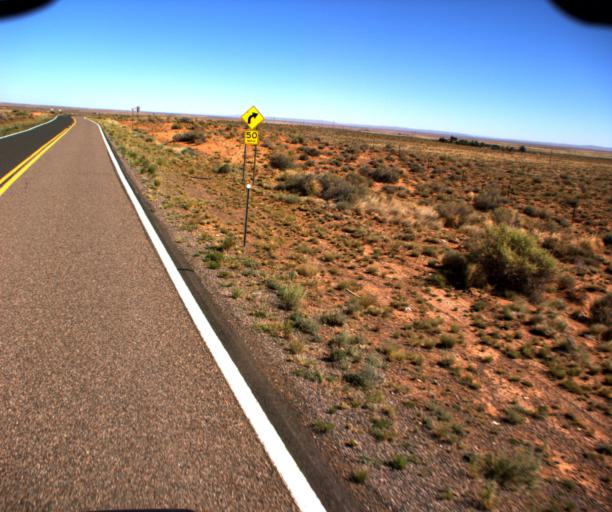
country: US
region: Arizona
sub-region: Coconino County
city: LeChee
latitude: 35.1157
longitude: -110.8721
